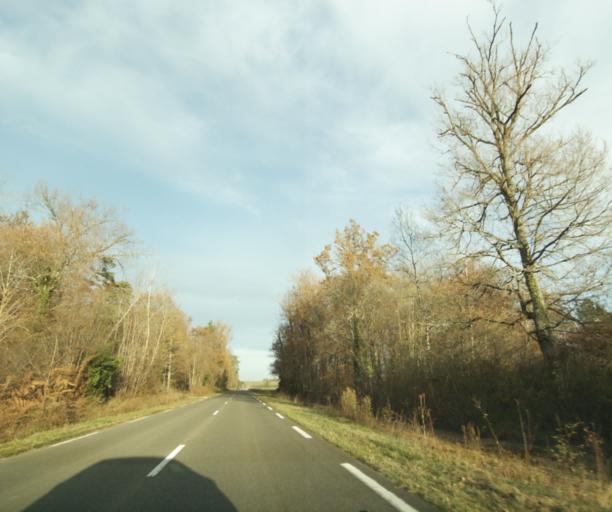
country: FR
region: Aquitaine
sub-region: Departement des Landes
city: Gabarret
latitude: 43.9595
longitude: -0.0151
